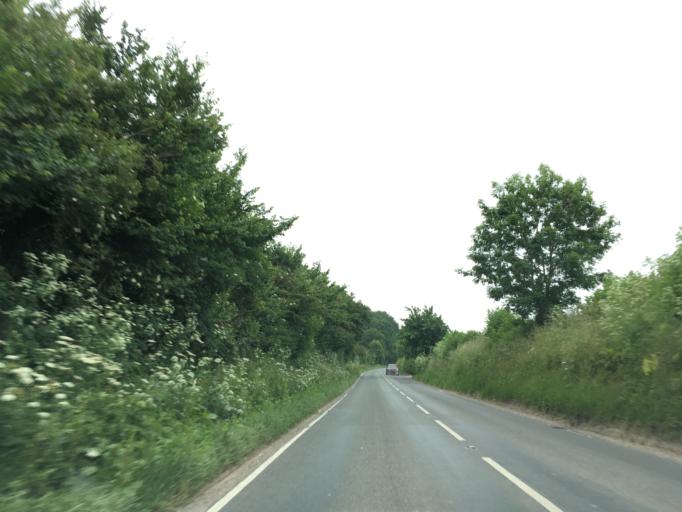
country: GB
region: England
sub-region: Gloucestershire
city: Stonehouse
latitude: 51.7643
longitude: -2.3488
